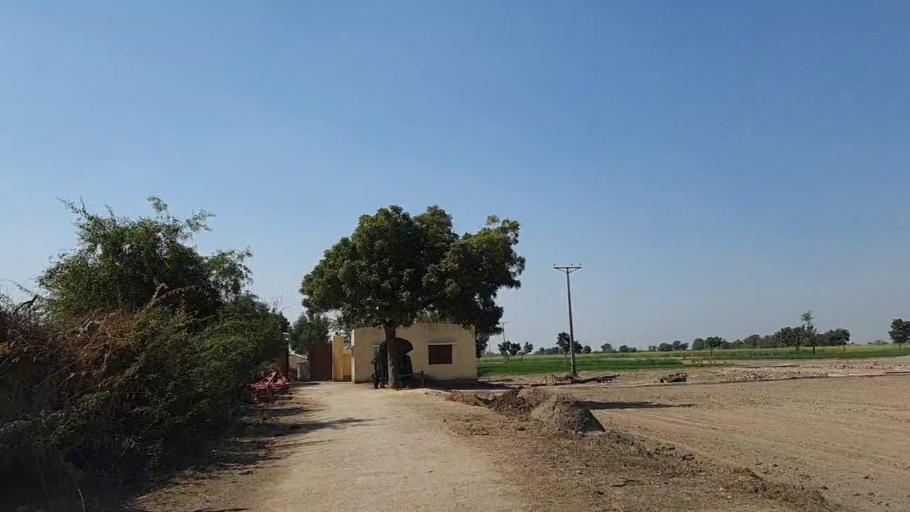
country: PK
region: Sindh
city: Samaro
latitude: 25.3949
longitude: 69.3831
